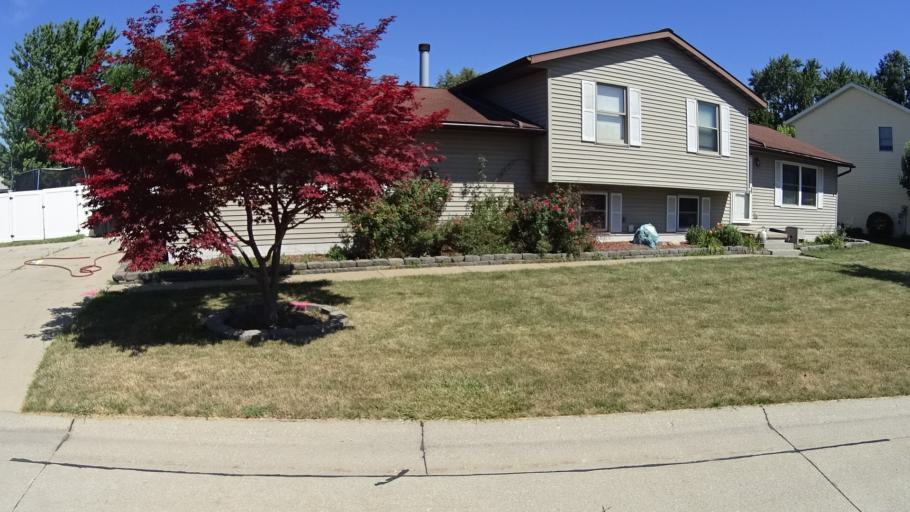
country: US
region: Ohio
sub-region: Erie County
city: Sandusky
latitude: 41.4105
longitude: -82.6872
